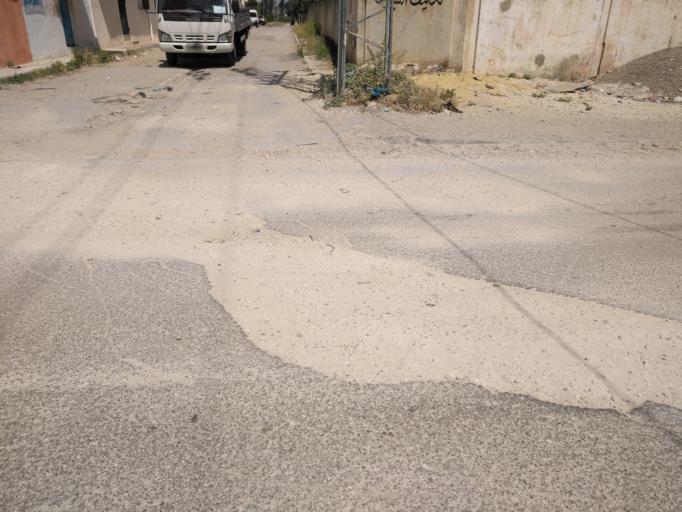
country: TN
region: Silyanah
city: Siliana
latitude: 36.0897
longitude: 9.3759
